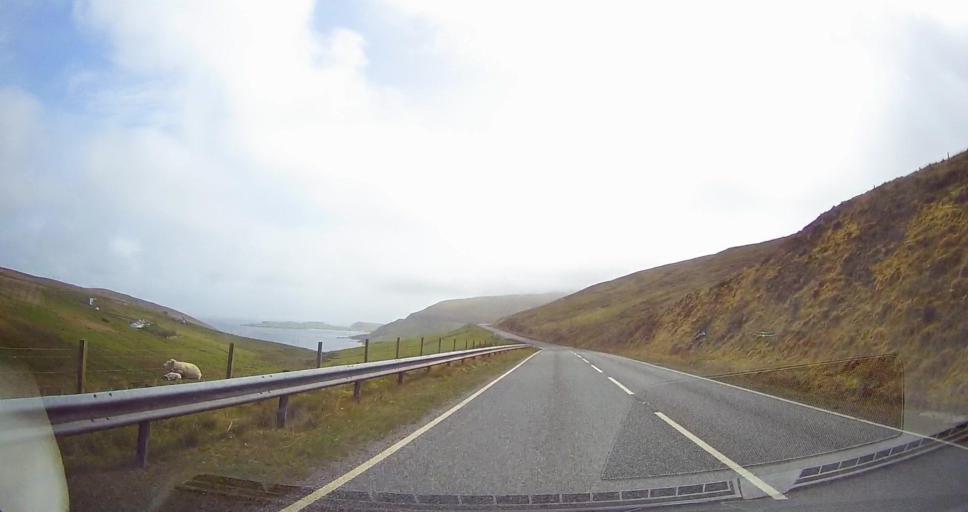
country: GB
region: Scotland
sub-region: Shetland Islands
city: Sandwick
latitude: 59.9997
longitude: -1.2792
